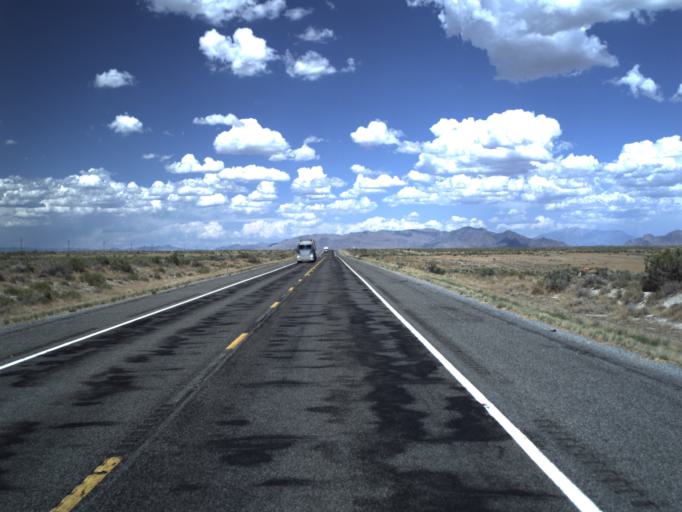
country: US
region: Utah
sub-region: Millard County
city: Delta
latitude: 39.4249
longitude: -112.4724
